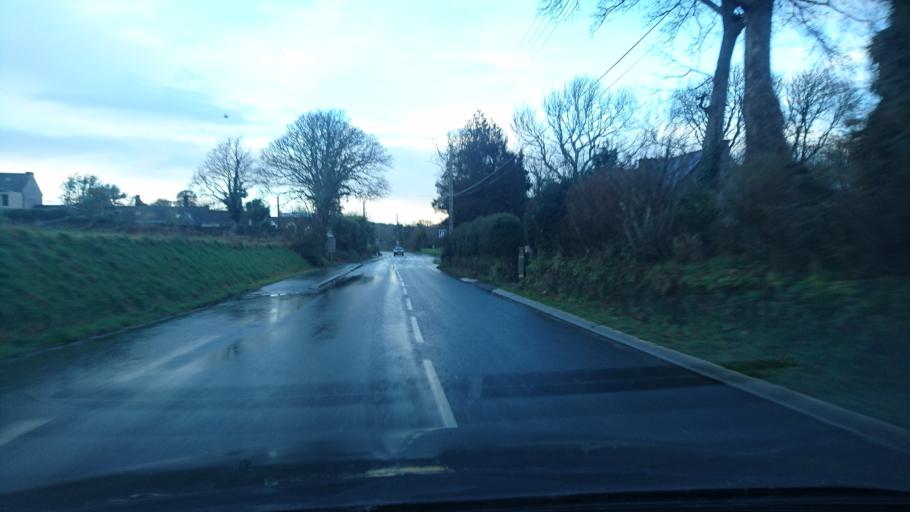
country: FR
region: Brittany
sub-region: Departement du Finistere
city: Guilers
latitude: 48.3989
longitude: -4.5398
